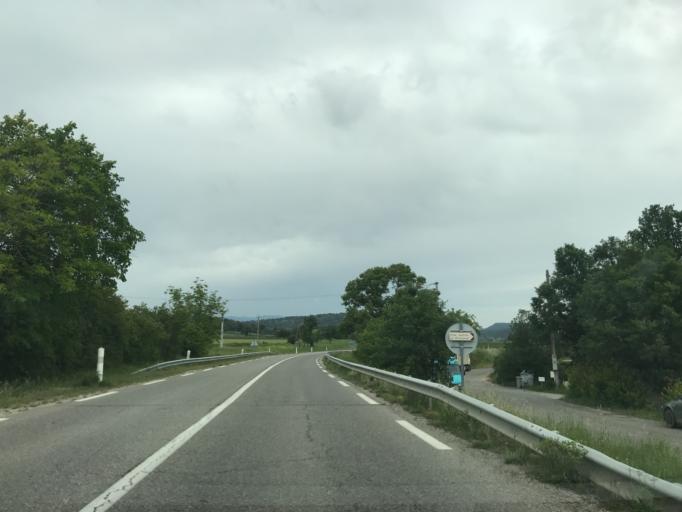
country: FR
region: Provence-Alpes-Cote d'Azur
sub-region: Departement des Alpes-de-Haute-Provence
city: Oraison
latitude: 43.9417
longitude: 5.8890
